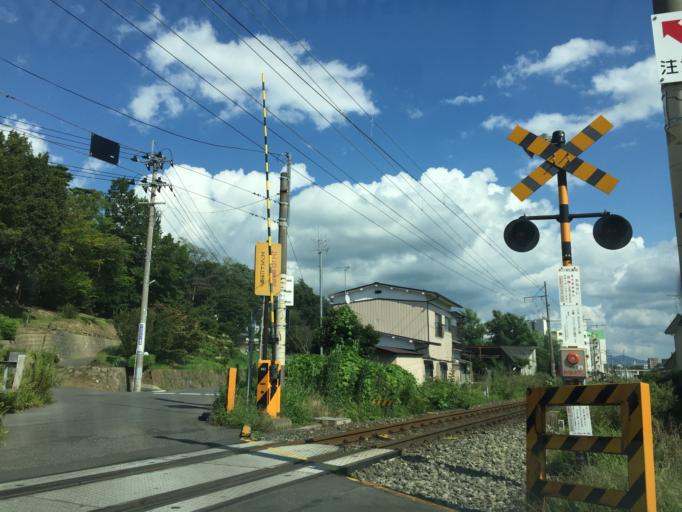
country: JP
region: Fukushima
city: Koriyama
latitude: 37.4106
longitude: 140.3820
